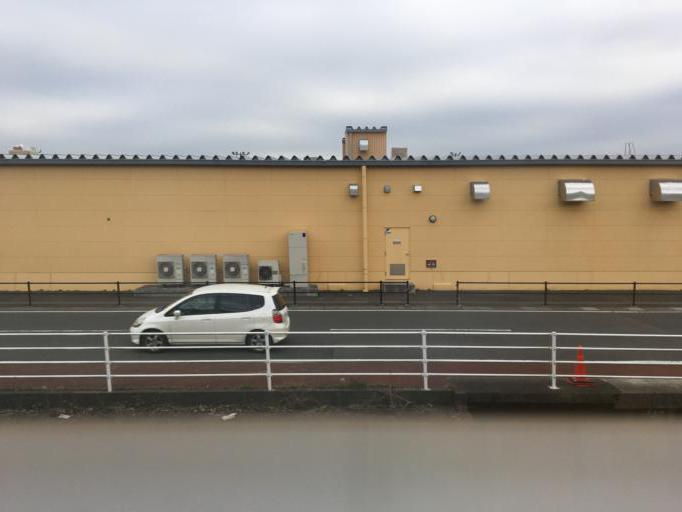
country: JP
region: Tochigi
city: Tochigi
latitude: 36.3481
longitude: 139.7030
